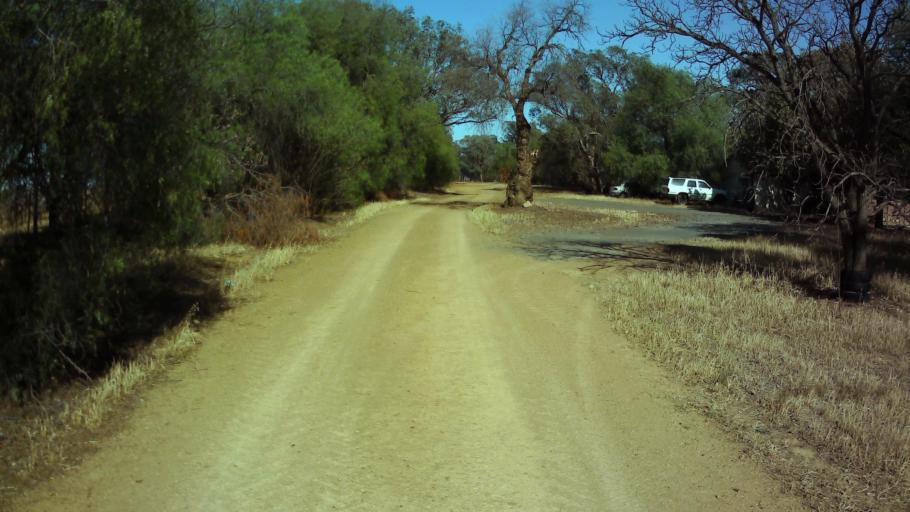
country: AU
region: New South Wales
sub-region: Weddin
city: Grenfell
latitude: -34.0469
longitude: 148.2754
